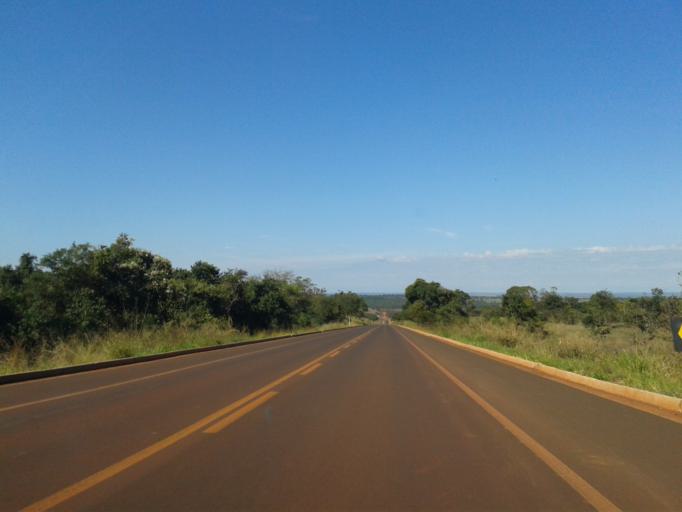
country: BR
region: Minas Gerais
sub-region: Ituiutaba
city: Ituiutaba
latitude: -19.0302
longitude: -49.5031
